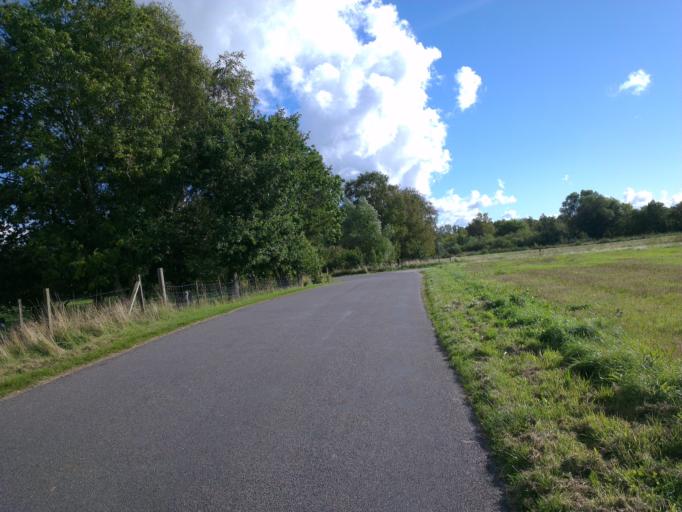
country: DK
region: Capital Region
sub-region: Frederikssund Kommune
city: Frederikssund
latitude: 55.7865
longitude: 12.0307
